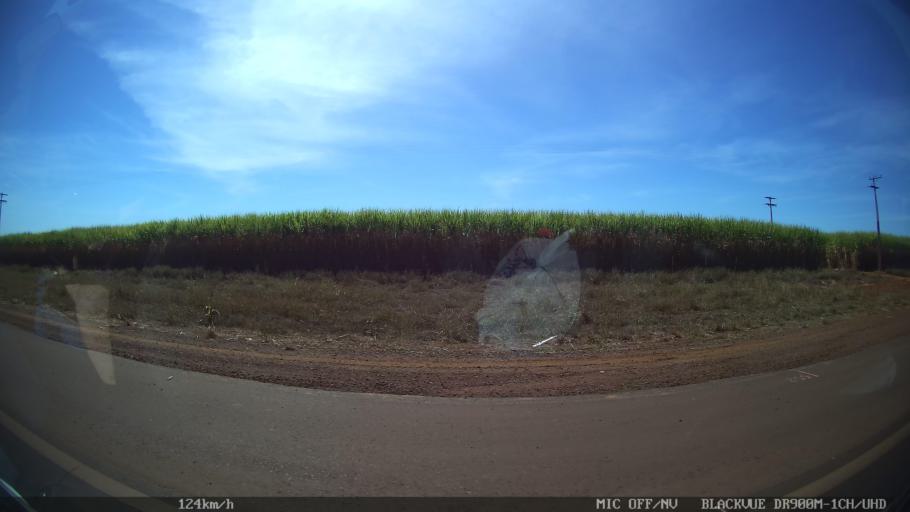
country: BR
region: Sao Paulo
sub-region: Ipua
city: Ipua
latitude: -20.5031
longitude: -47.9412
